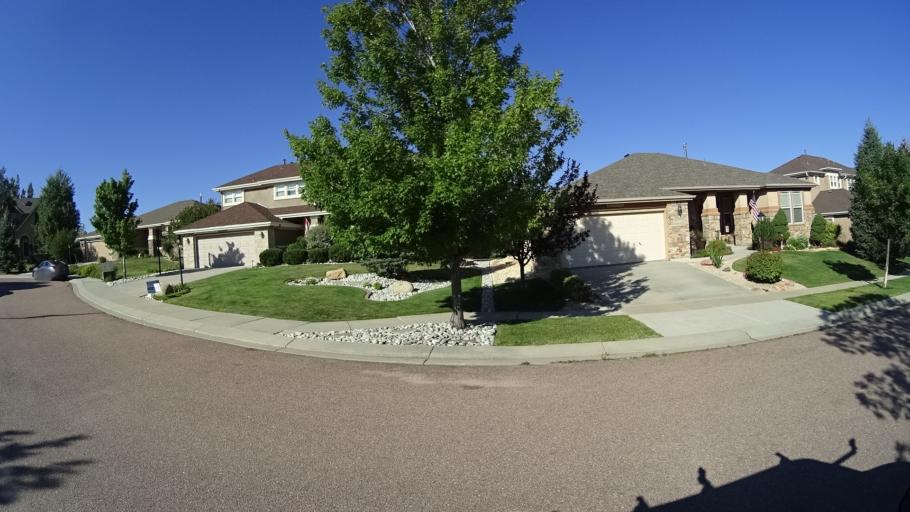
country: US
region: Colorado
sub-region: El Paso County
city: Black Forest
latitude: 38.9795
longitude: -104.7617
